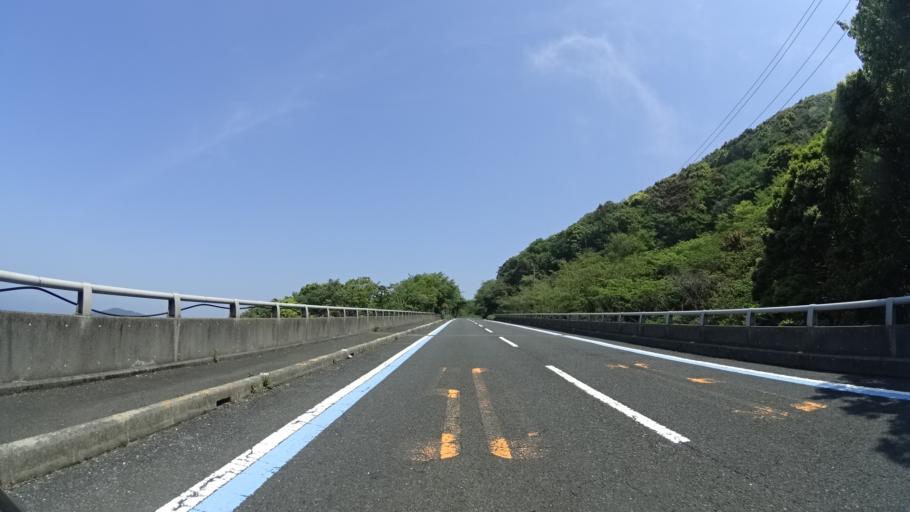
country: JP
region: Ehime
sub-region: Nishiuwa-gun
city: Ikata-cho
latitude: 33.4125
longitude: 132.1722
